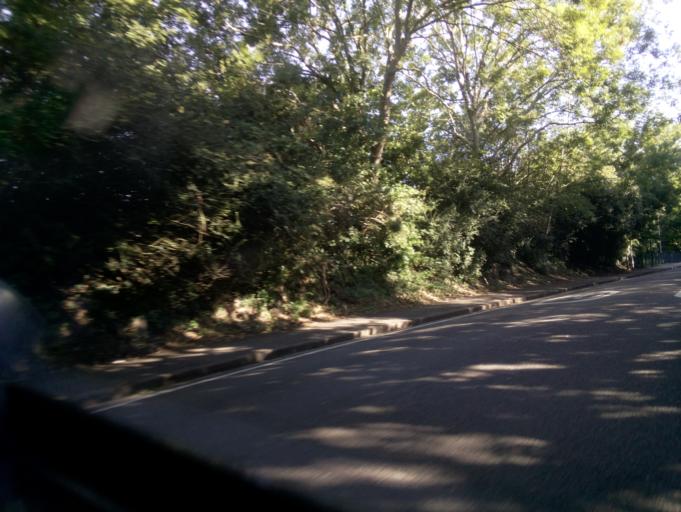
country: GB
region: England
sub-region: South Gloucestershire
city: Kingswood
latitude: 51.4484
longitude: -2.5462
